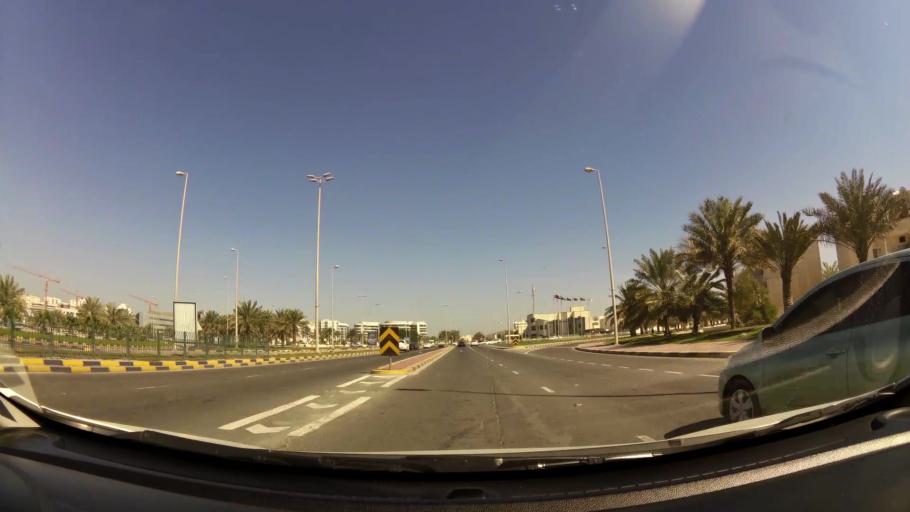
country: BH
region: Muharraq
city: Al Muharraq
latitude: 26.2593
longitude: 50.6032
